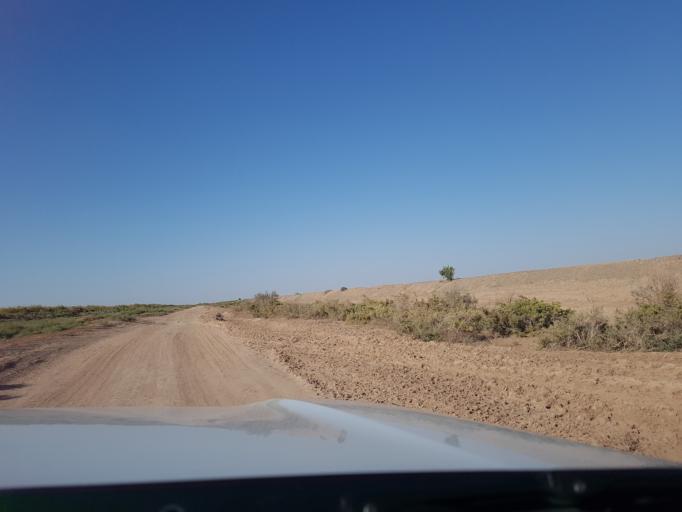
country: IR
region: Razavi Khorasan
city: Sarakhs
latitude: 36.9717
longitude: 61.3840
